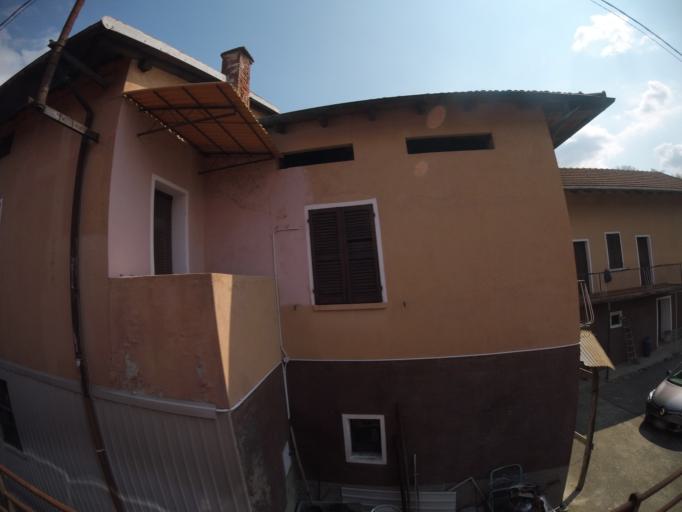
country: IT
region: Piedmont
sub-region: Provincia di Novara
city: Pettenasco
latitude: 45.8256
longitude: 8.3998
